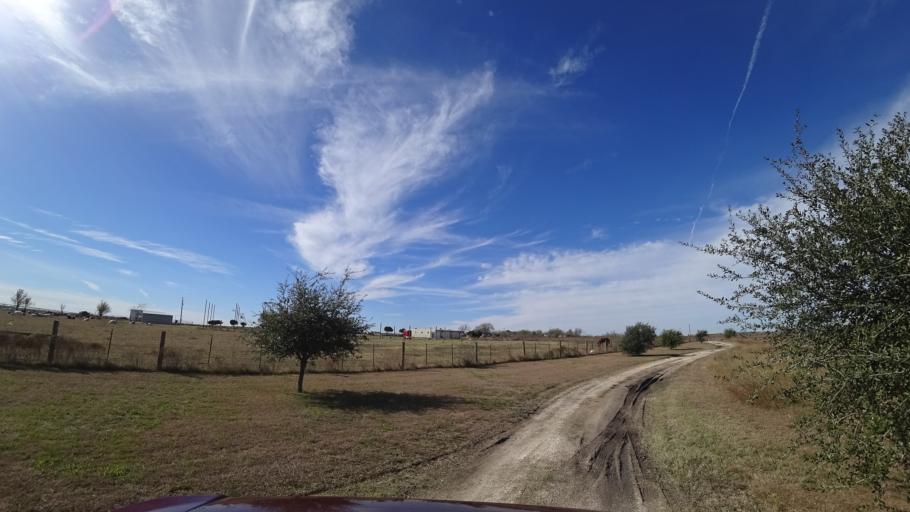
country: US
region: Texas
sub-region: Travis County
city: Onion Creek
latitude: 30.1135
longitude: -97.6817
